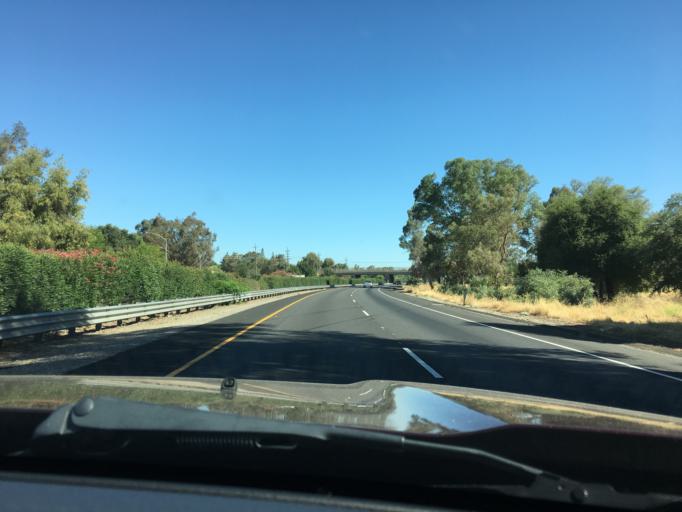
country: US
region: California
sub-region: San Joaquin County
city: Lodi
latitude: 38.1426
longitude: -121.2602
